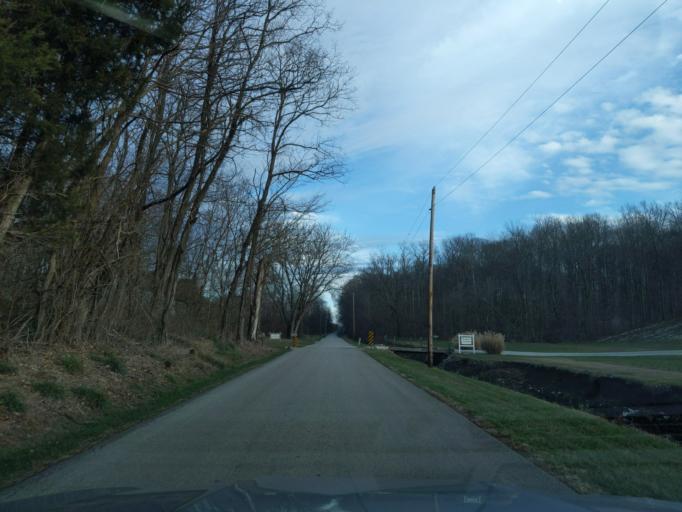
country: US
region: Indiana
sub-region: Decatur County
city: Westport
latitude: 39.2196
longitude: -85.5047
